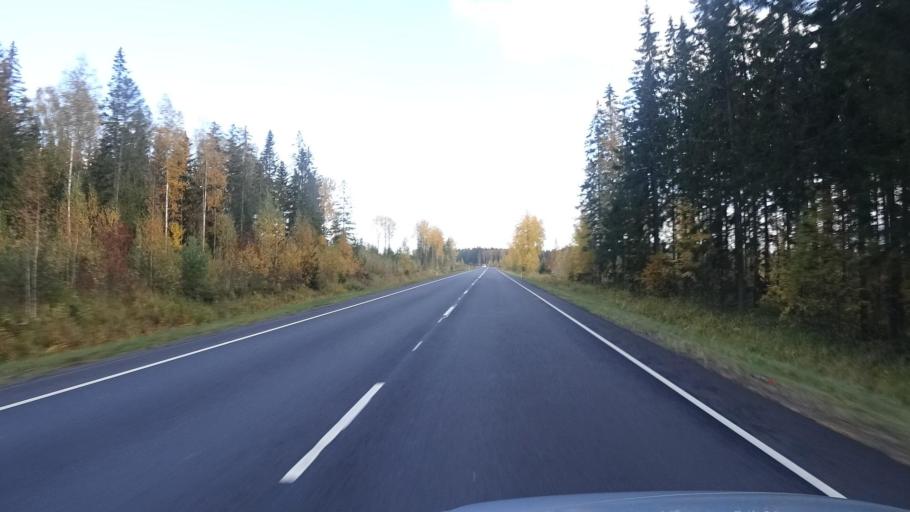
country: FI
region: Satakunta
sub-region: Rauma
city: Eura
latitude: 61.1108
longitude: 22.2070
